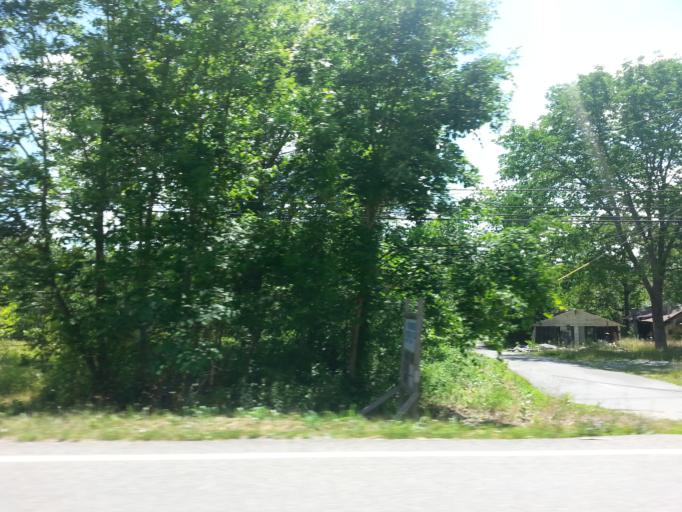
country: US
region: Virginia
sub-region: Lee County
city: Pennington Gap
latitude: 36.7209
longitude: -82.9835
